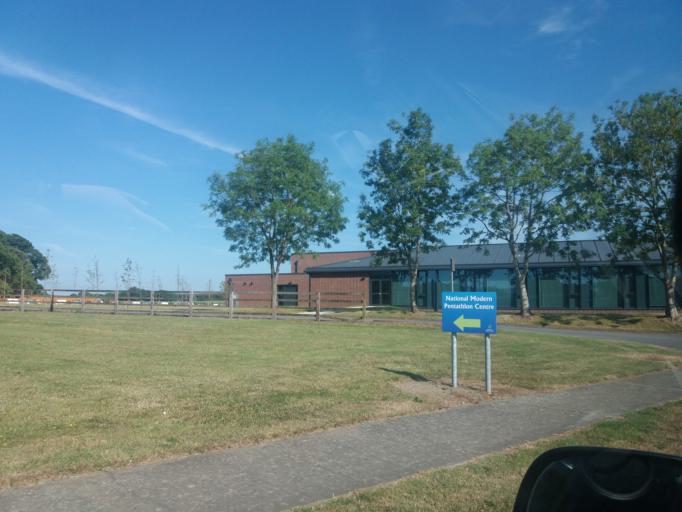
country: IE
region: Leinster
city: Castleknock
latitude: 53.3938
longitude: -6.3558
